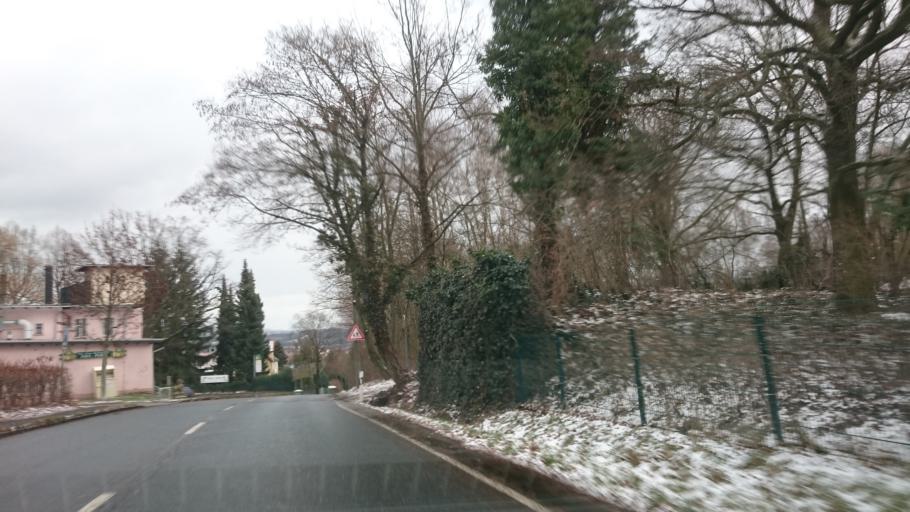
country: DE
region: Saxony
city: Weissenborn
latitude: 50.7276
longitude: 12.4554
